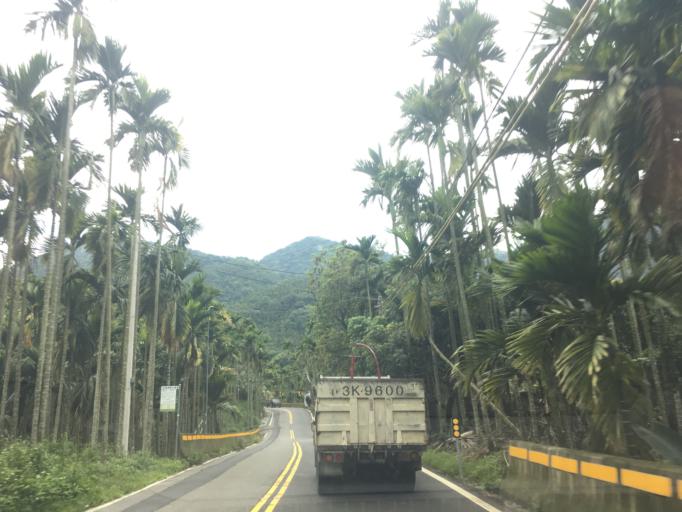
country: TW
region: Taiwan
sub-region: Chiayi
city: Jiayi Shi
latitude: 23.5591
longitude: 120.5784
